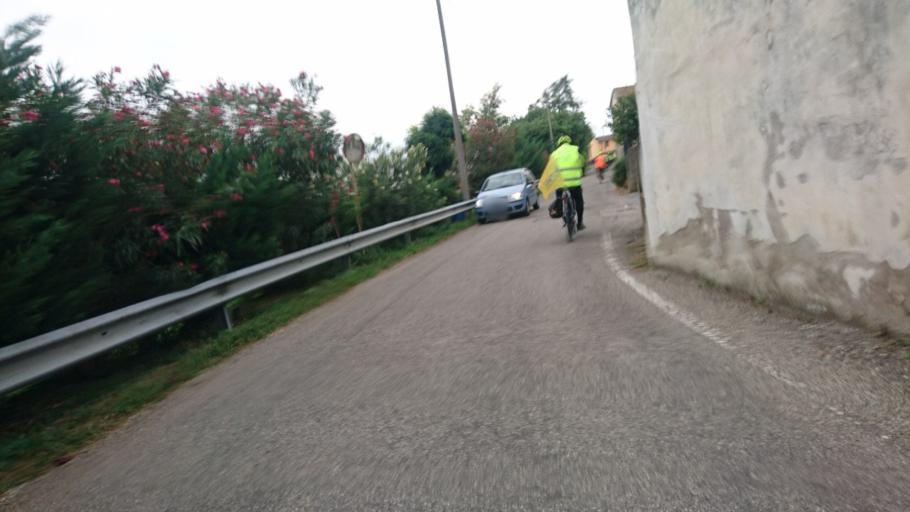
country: IT
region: Veneto
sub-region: Provincia di Verona
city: San Giovanni Lupatoto
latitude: 45.4115
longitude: 11.0591
